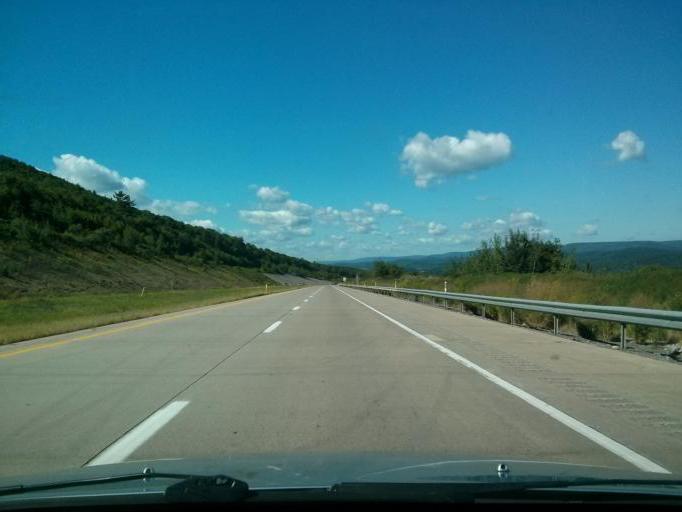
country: US
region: Pennsylvania
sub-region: Centre County
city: Stormstown
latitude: 40.8277
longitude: -77.9939
